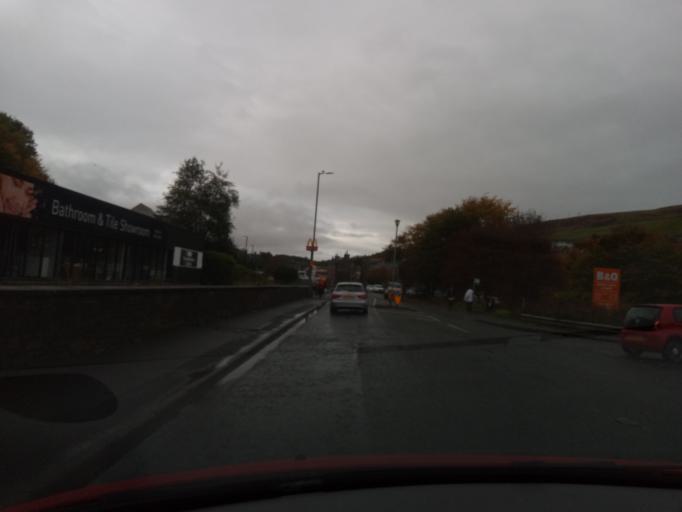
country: GB
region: Scotland
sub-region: The Scottish Borders
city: Galashiels
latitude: 55.6200
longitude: -2.8147
